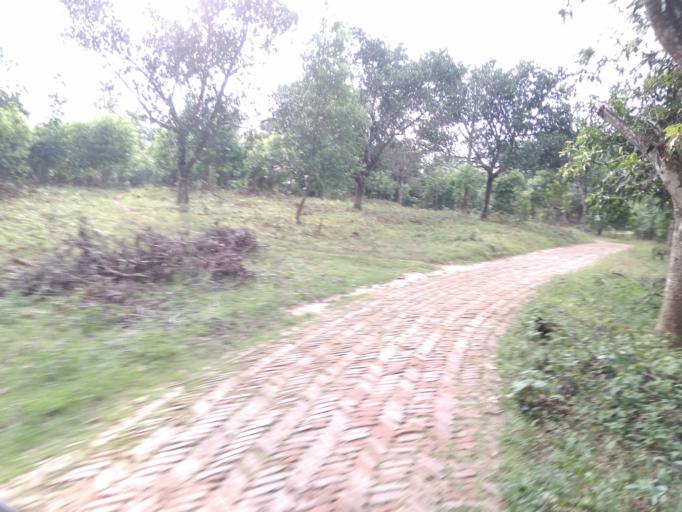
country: BD
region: Chittagong
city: Manikchari
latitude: 22.9298
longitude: 91.9123
